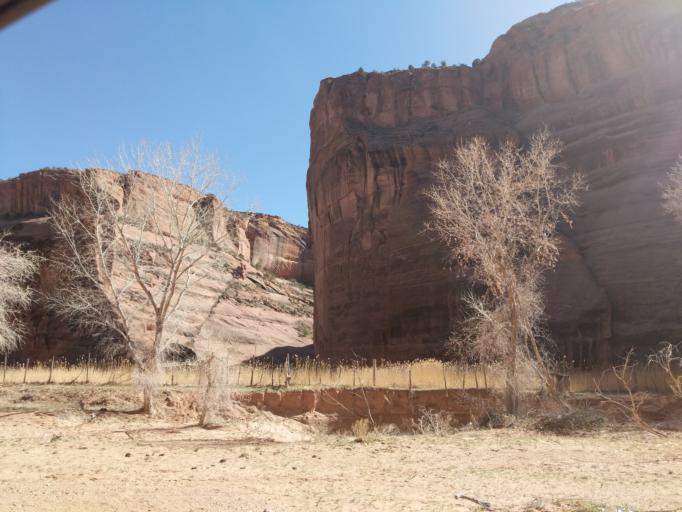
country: US
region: Arizona
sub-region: Apache County
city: Chinle
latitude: 36.1560
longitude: -109.4495
